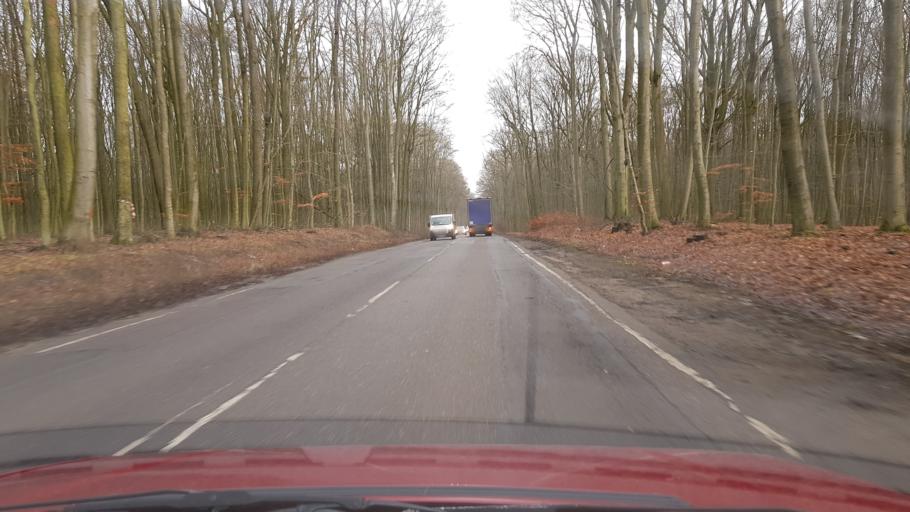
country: PL
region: West Pomeranian Voivodeship
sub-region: Powiat policki
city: Police
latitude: 53.5290
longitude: 14.5723
